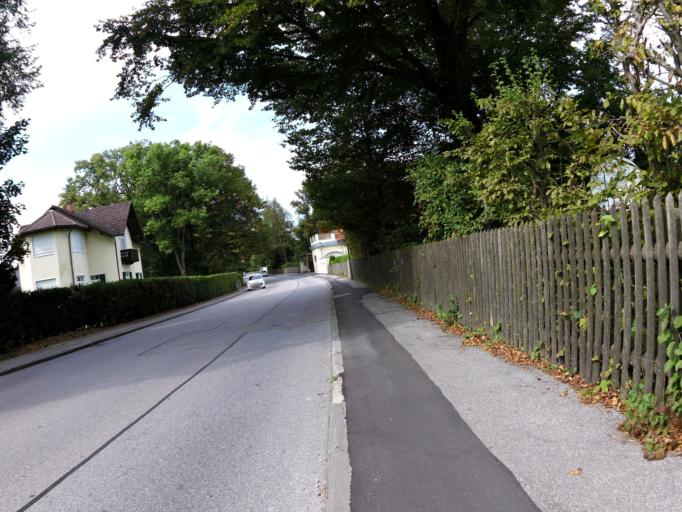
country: DE
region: Bavaria
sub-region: Upper Bavaria
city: Seeshaupt
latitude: 47.8222
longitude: 11.3103
